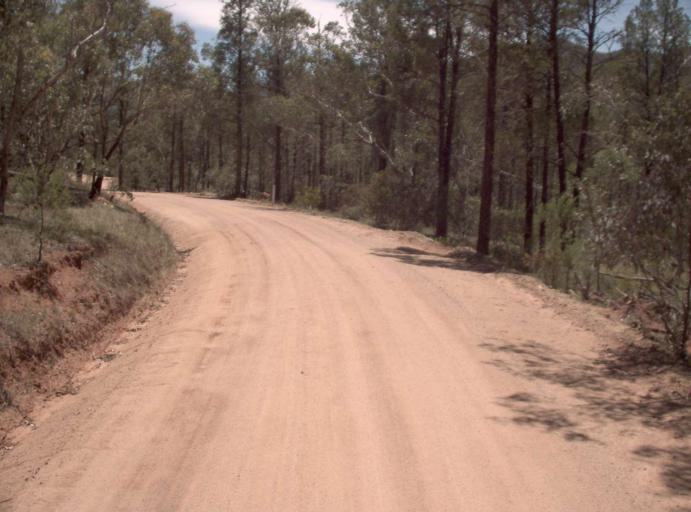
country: AU
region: New South Wales
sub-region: Snowy River
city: Jindabyne
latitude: -36.8937
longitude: 148.4227
